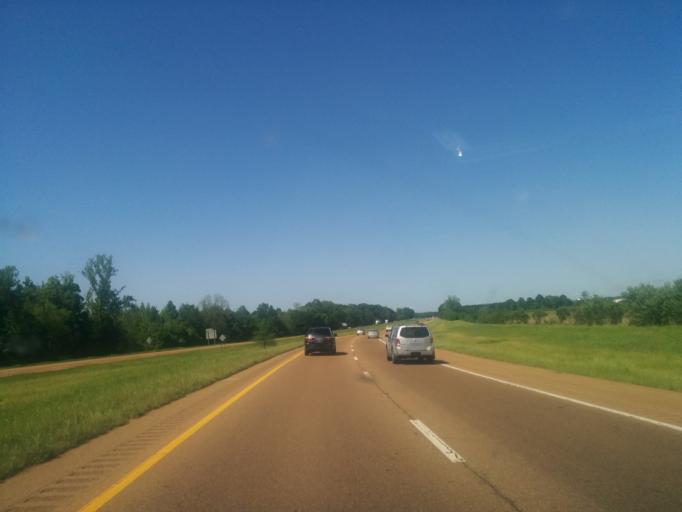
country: US
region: Mississippi
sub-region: Madison County
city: Madison
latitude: 32.4860
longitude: -90.1301
